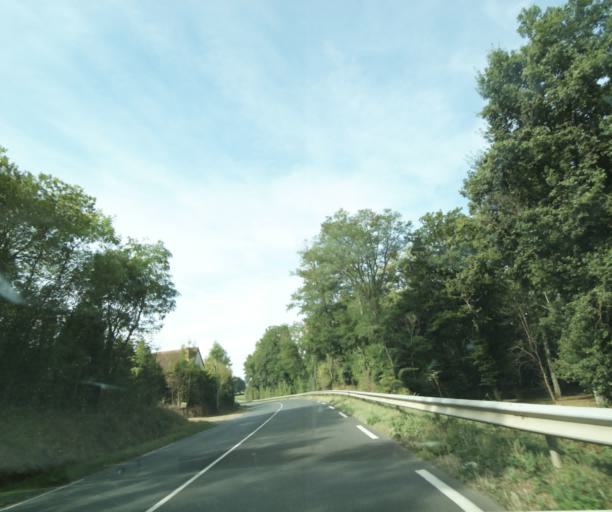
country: FR
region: Auvergne
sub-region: Departement de l'Allier
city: Creuzier-le-Vieux
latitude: 46.1826
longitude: 3.4729
